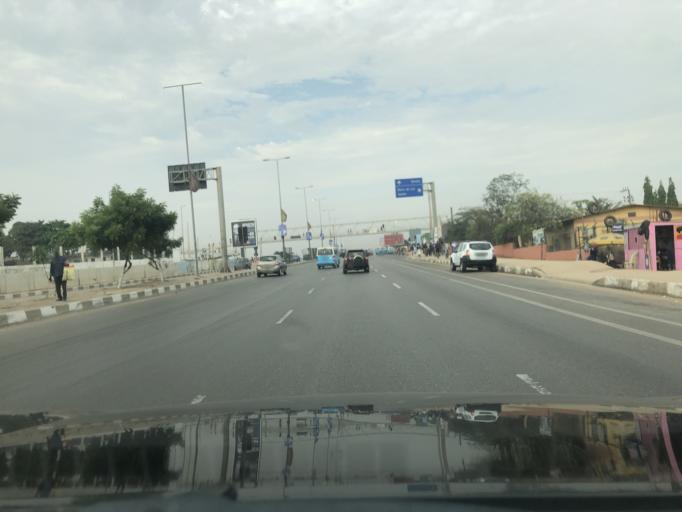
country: AO
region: Luanda
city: Luanda
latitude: -8.8686
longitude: 13.2125
